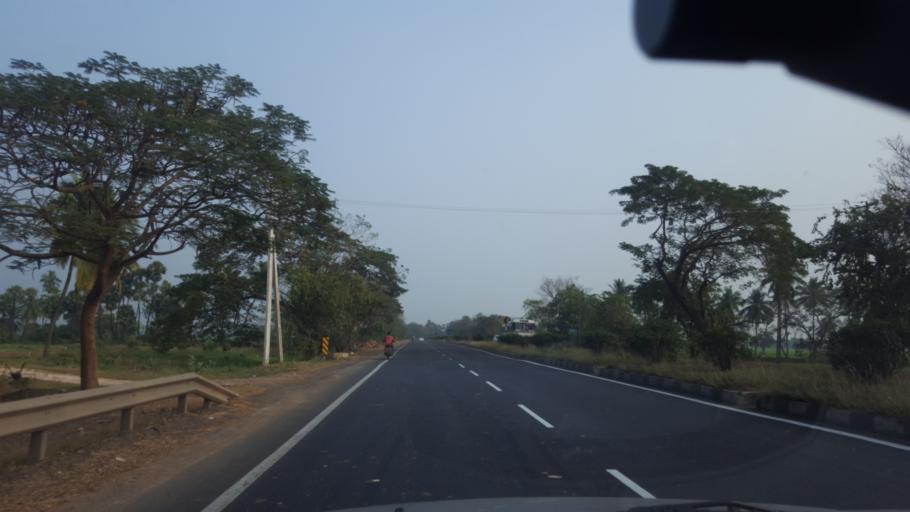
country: IN
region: Andhra Pradesh
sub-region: West Godavari
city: Tadepallegudem
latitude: 16.7929
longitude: 81.5992
